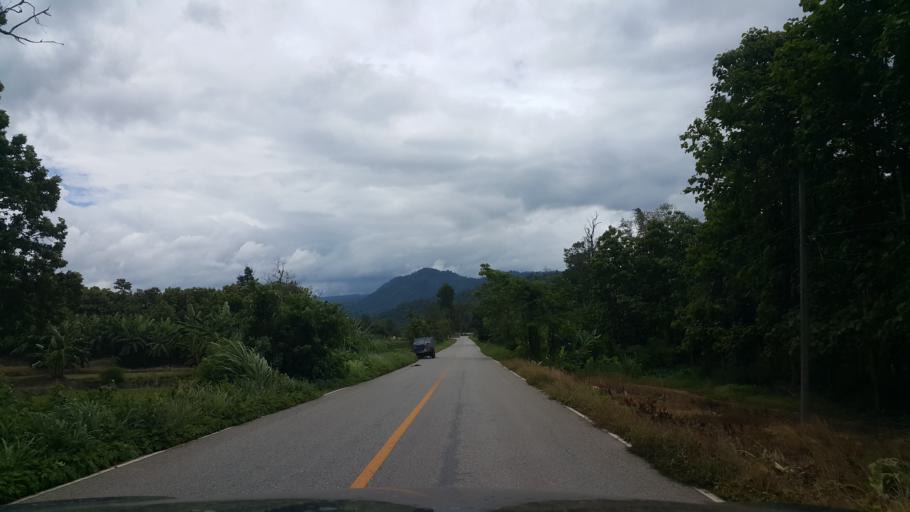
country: TH
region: Phitsanulok
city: Chat Trakan
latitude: 17.3758
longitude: 100.7469
